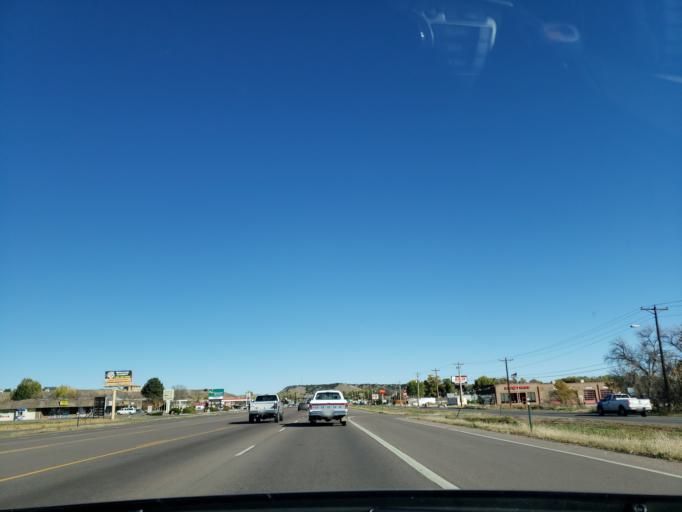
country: US
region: Colorado
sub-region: Fremont County
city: Lincoln Park
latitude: 38.4469
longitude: -105.1983
